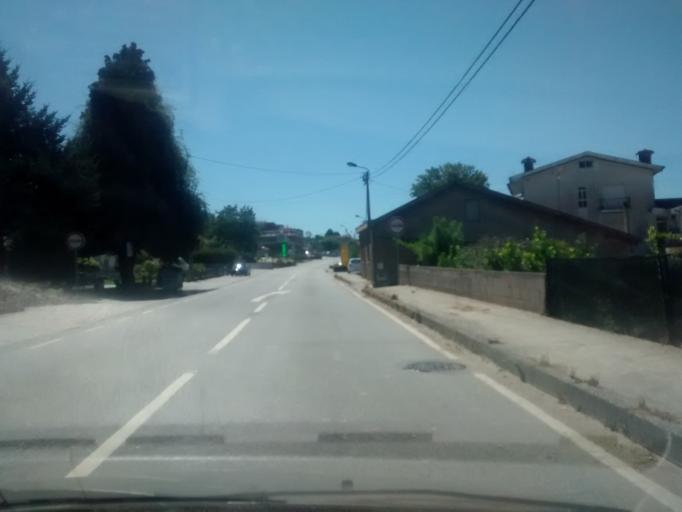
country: PT
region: Braga
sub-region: Braga
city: Oliveira
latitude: 41.5336
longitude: -8.5075
